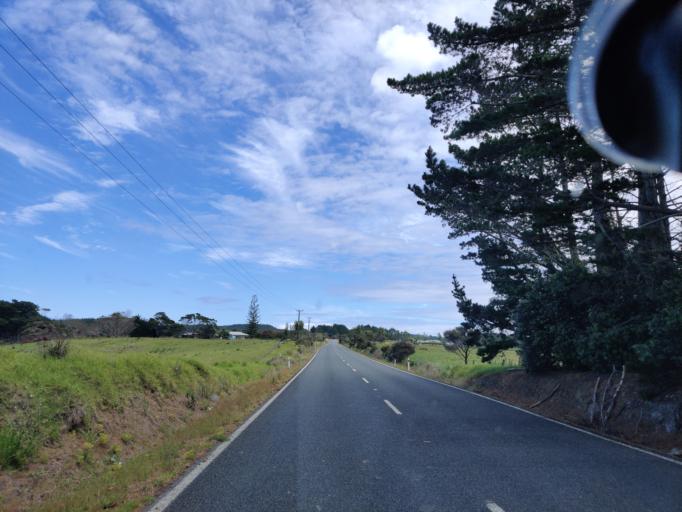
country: NZ
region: Northland
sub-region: Far North District
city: Kaitaia
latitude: -34.6702
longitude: 172.9842
